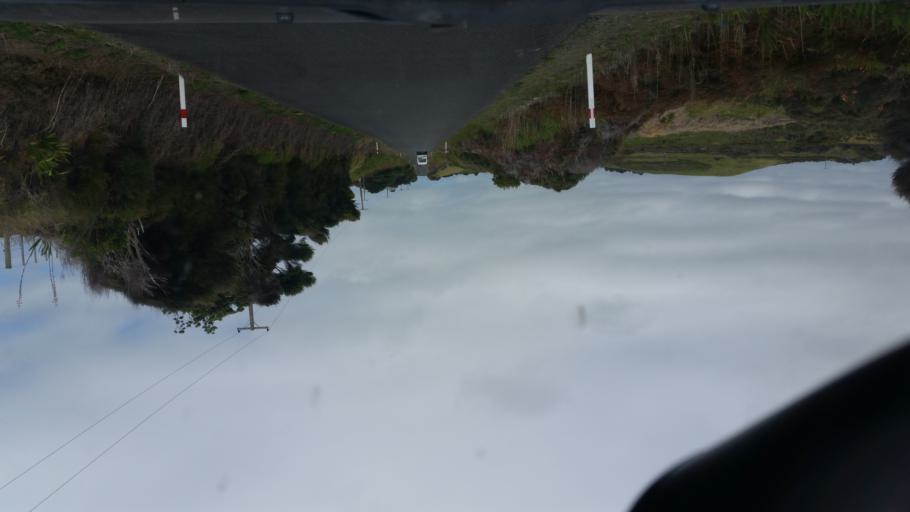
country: NZ
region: Northland
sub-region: Kaipara District
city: Dargaville
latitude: -35.8119
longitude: 173.6385
